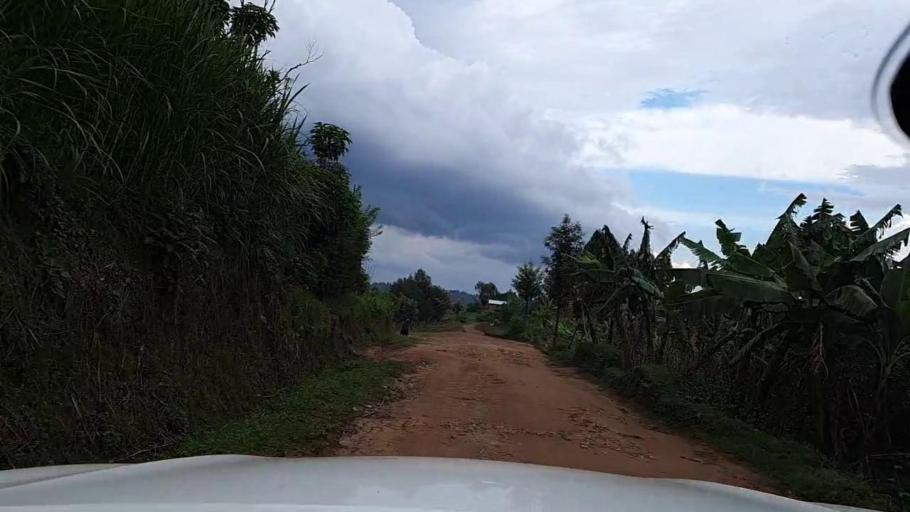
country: BI
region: Kayanza
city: Kayanza
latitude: -2.7957
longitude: 29.5161
